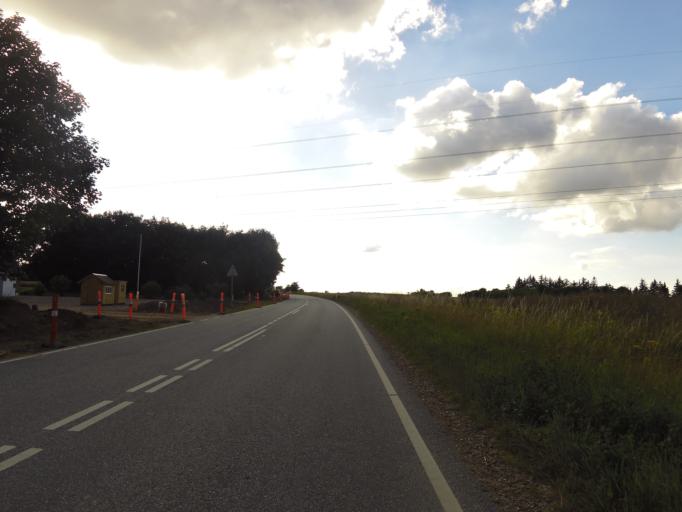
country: DK
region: South Denmark
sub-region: Haderslev Kommune
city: Vojens
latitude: 55.1974
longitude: 9.3250
